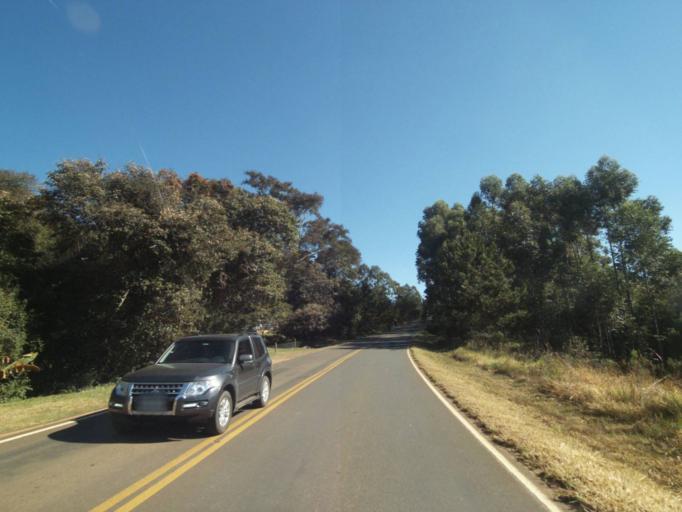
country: BR
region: Parana
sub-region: Tibagi
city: Tibagi
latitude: -24.4989
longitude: -50.4568
